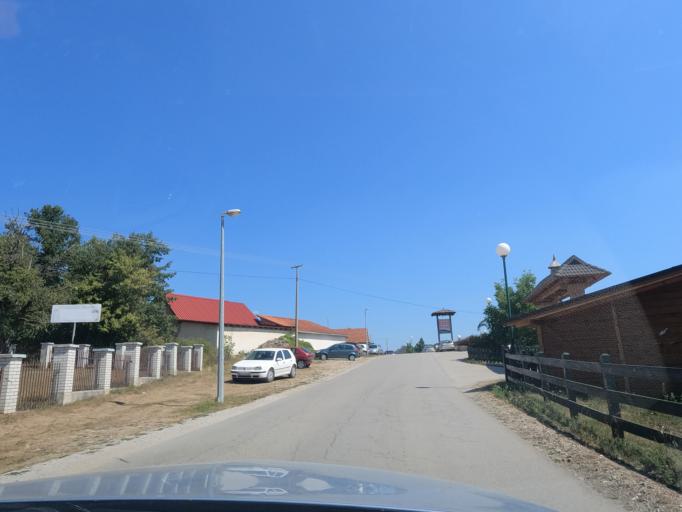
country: RS
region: Central Serbia
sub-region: Zlatiborski Okrug
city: Cajetina
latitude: 43.7888
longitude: 19.7678
